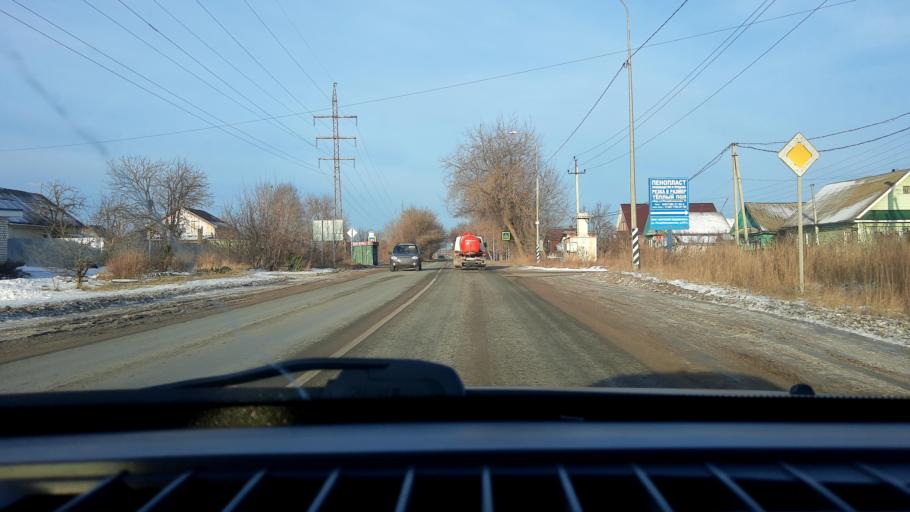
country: RU
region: Nizjnij Novgorod
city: Bor
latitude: 56.3658
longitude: 44.0712
